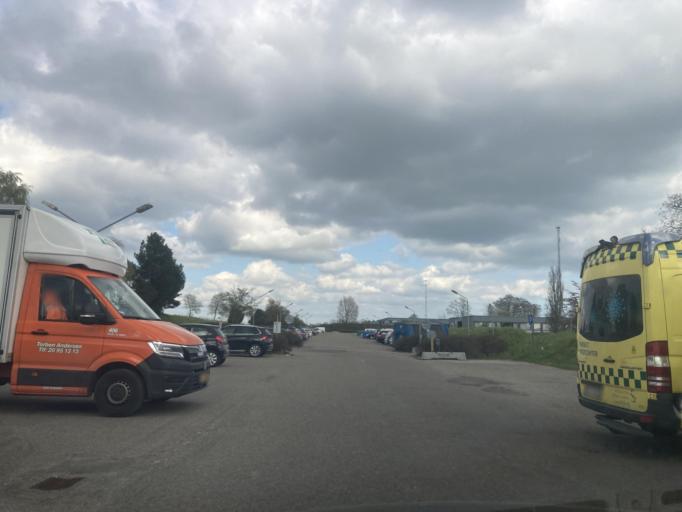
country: DK
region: Zealand
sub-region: Solrod Kommune
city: Havdrup
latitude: 55.5845
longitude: 12.1131
